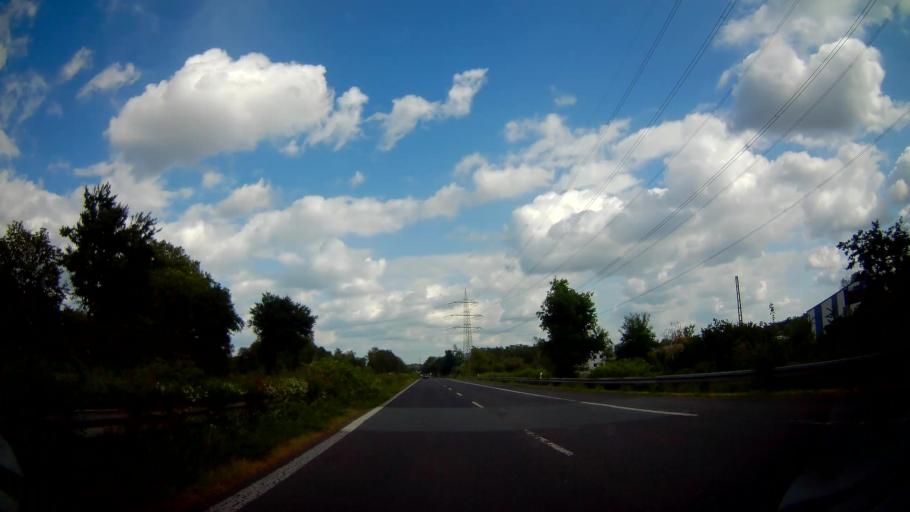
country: DE
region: North Rhine-Westphalia
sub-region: Regierungsbezirk Munster
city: Bottrop
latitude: 51.4908
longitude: 6.9579
